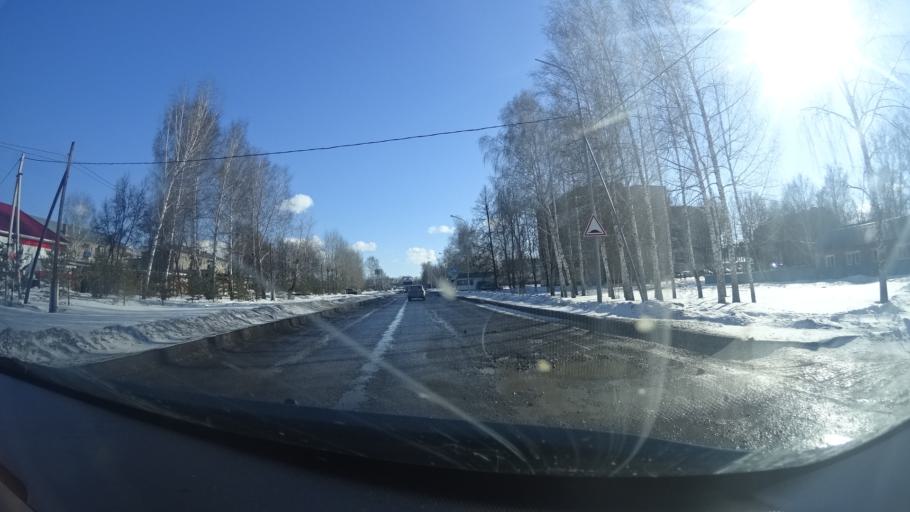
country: RU
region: Bashkortostan
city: Chishmy
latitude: 54.5886
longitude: 55.3696
